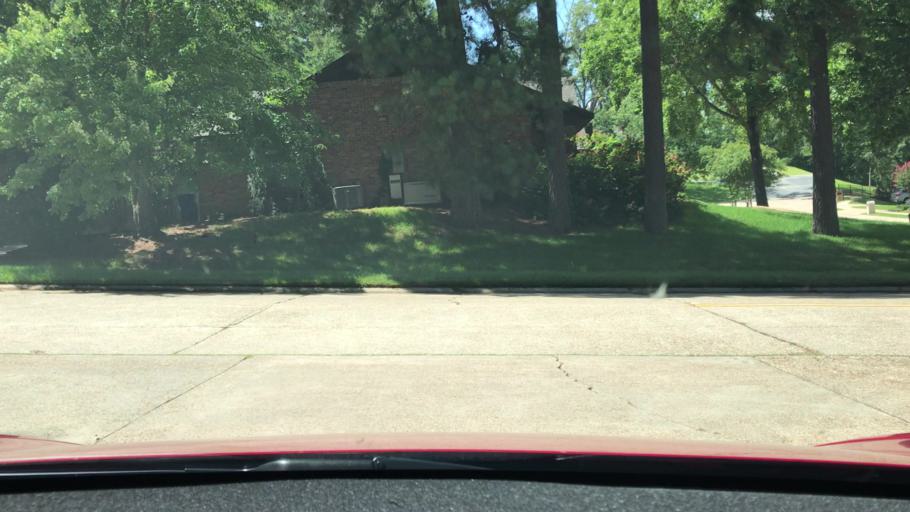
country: US
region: Louisiana
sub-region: Bossier Parish
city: Bossier City
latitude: 32.4250
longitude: -93.7286
